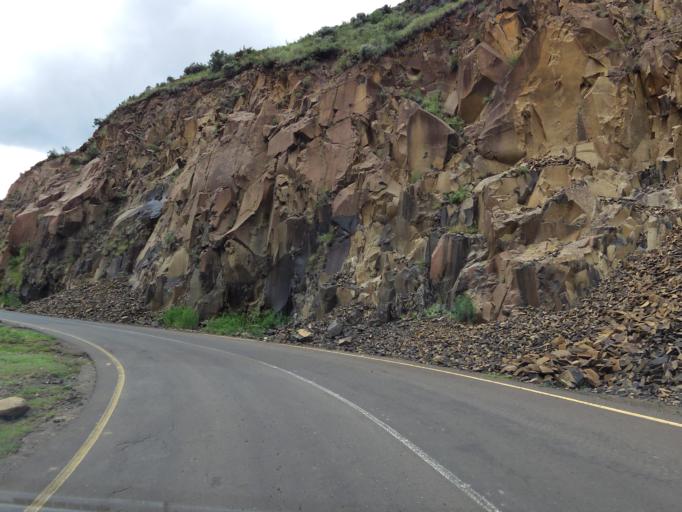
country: LS
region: Butha-Buthe
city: Butha-Buthe
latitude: -29.0549
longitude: 28.3457
